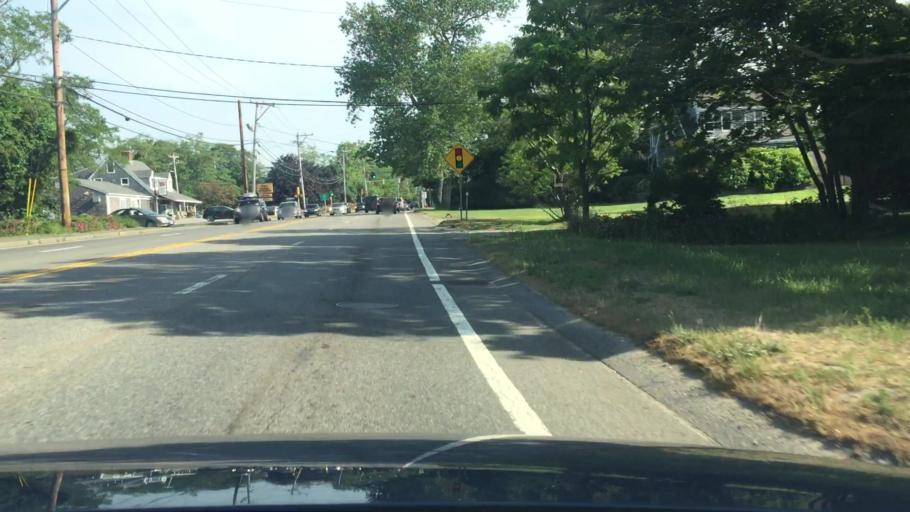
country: US
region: Massachusetts
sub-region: Barnstable County
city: Eastham
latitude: 41.8290
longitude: -69.9734
